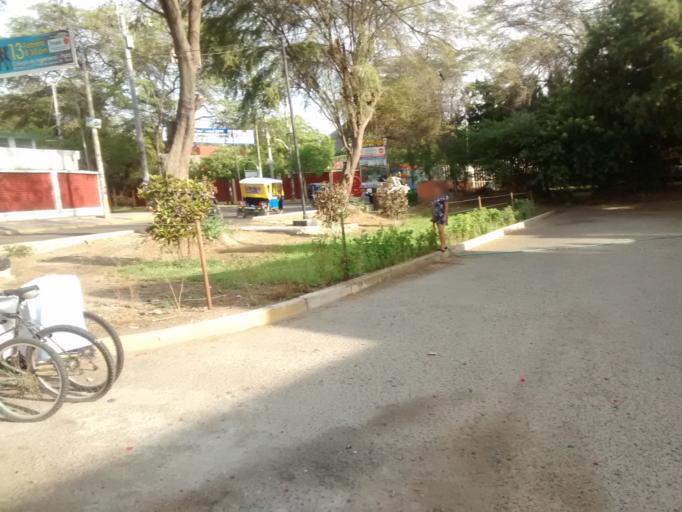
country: PE
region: Piura
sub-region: Provincia de Piura
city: Piura
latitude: -5.1747
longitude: -80.6279
